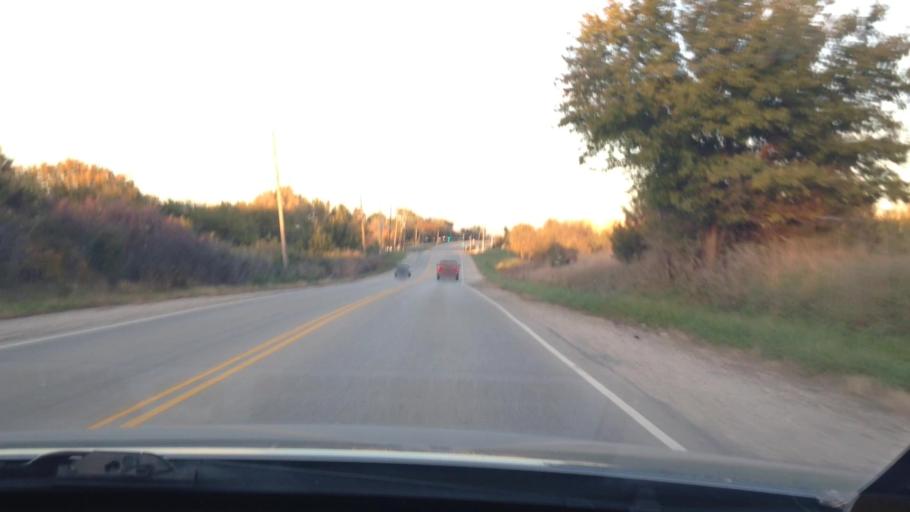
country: US
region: Kansas
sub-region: Johnson County
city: Olathe
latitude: 38.8626
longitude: -94.8484
